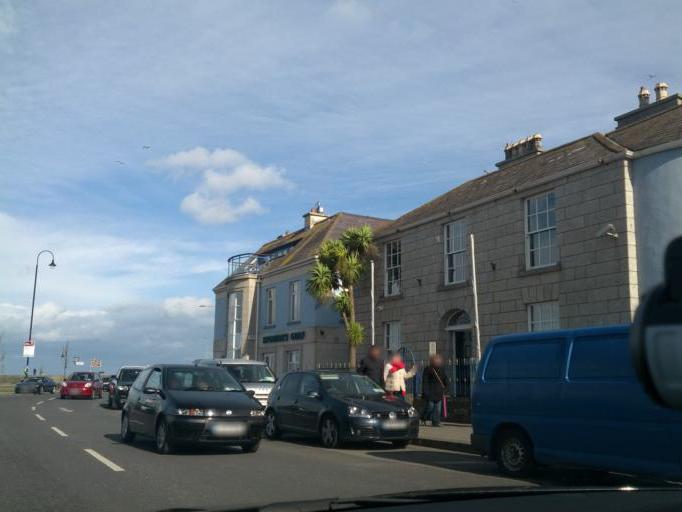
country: IE
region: Leinster
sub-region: Fingal County
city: Howth
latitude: 53.3881
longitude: -6.0658
